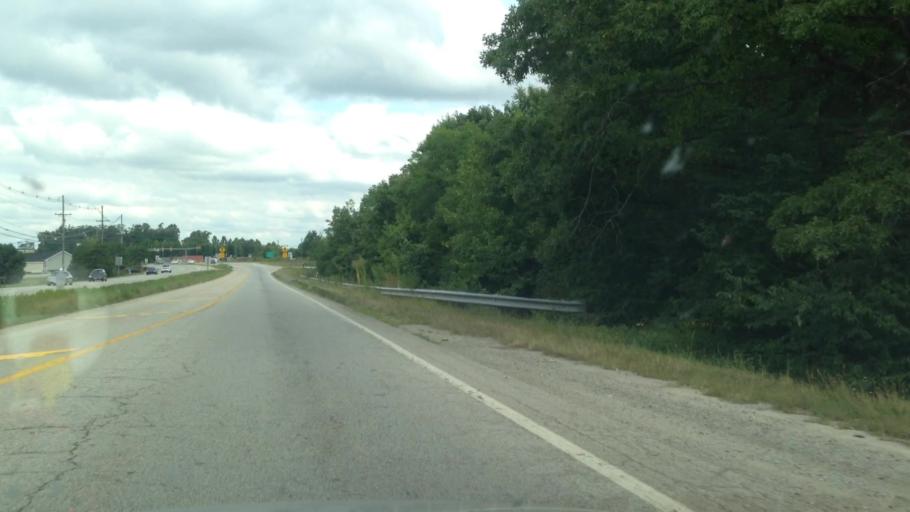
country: US
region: Virginia
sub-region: Pittsylvania County
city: Mount Hermon
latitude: 36.6934
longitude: -79.3669
